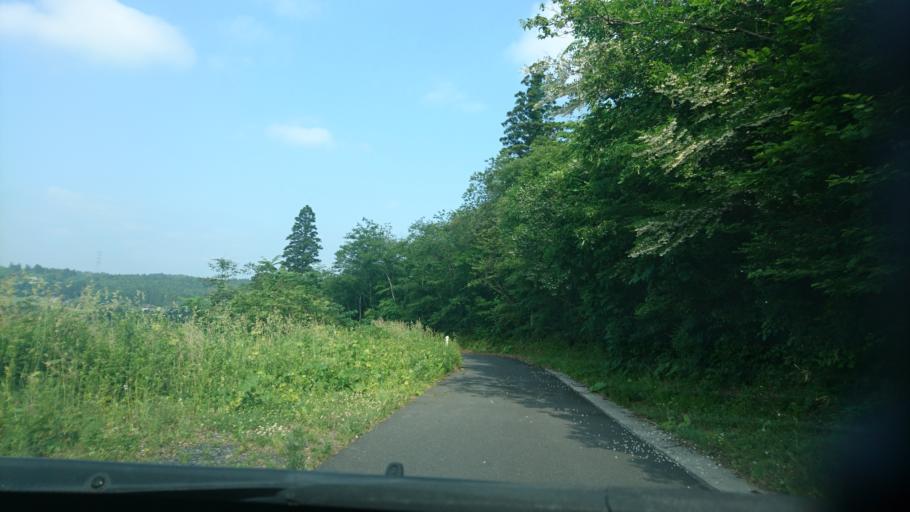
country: JP
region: Iwate
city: Ichinoseki
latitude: 38.9044
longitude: 141.2328
